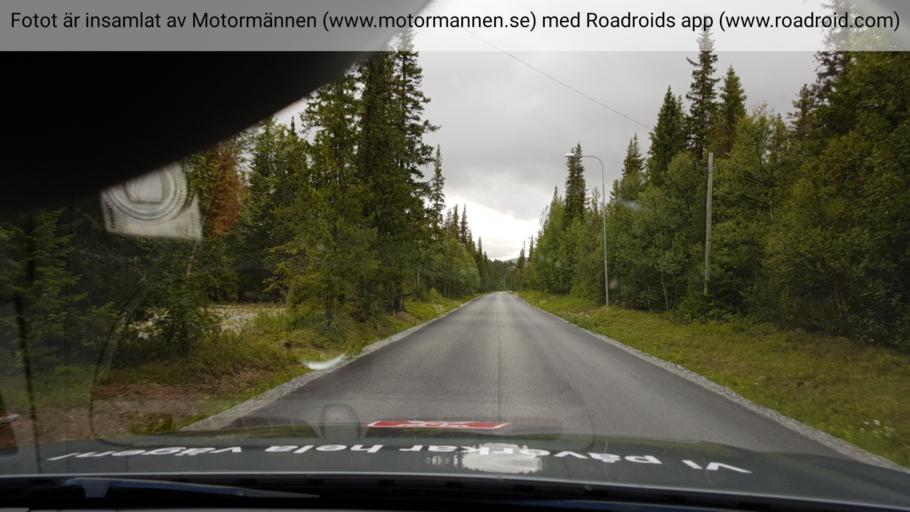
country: SE
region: Jaemtland
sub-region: Are Kommun
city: Are
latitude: 62.8553
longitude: 12.7706
